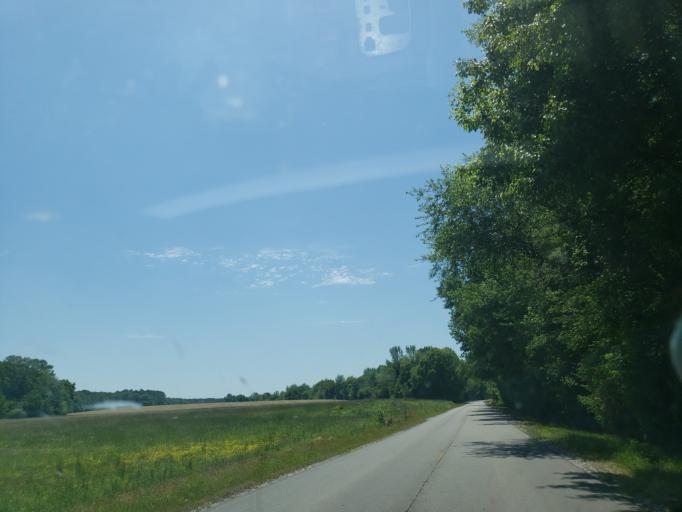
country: US
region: Alabama
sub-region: Madison County
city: Harvest
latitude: 34.9059
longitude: -86.7314
